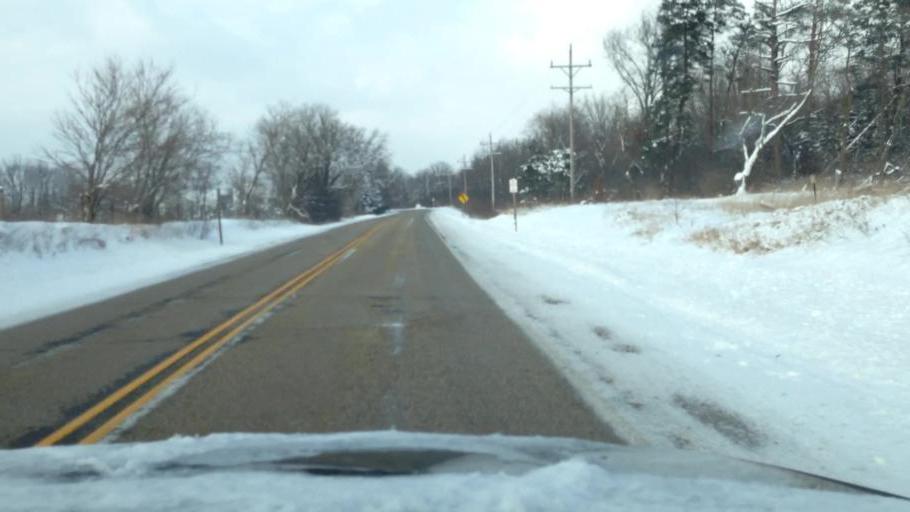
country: US
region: Wisconsin
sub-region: Walworth County
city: East Troy
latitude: 42.8380
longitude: -88.4242
